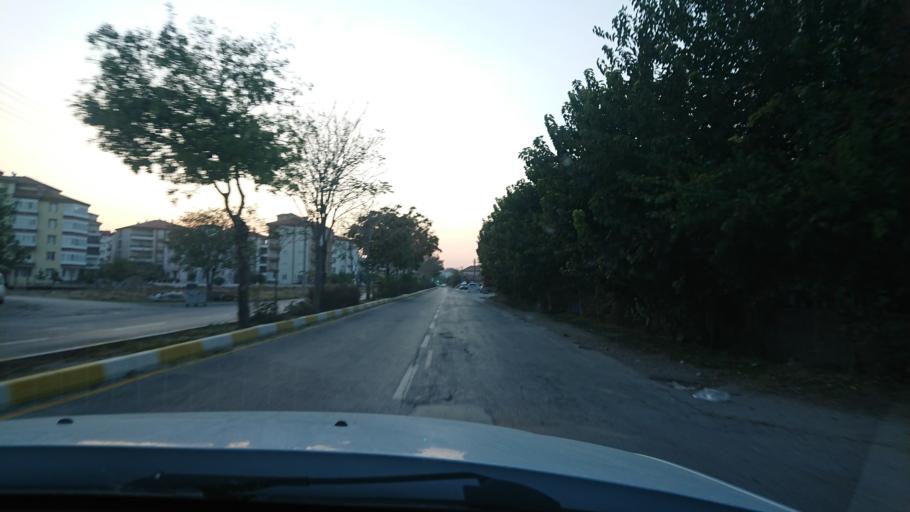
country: TR
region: Aksaray
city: Aksaray
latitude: 38.3604
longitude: 34.0120
